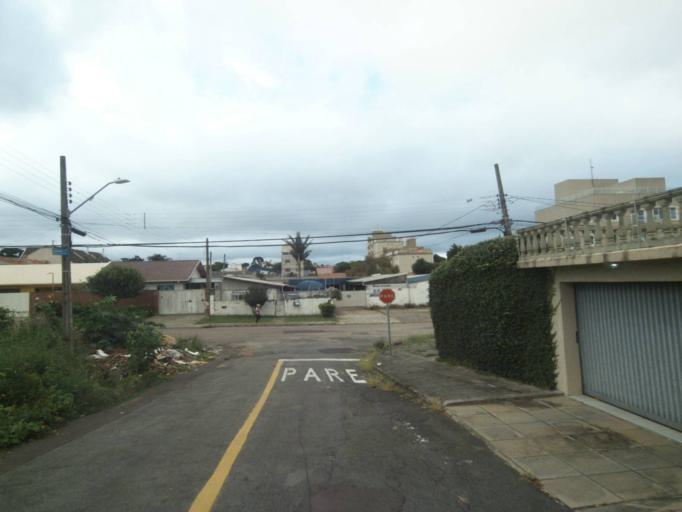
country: BR
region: Parana
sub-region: Pinhais
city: Pinhais
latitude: -25.4576
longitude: -49.2185
